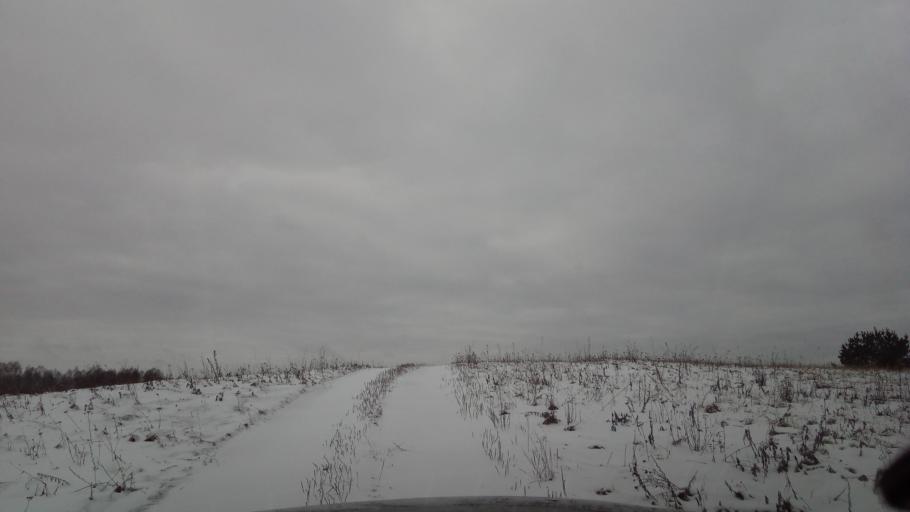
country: LT
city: Zarasai
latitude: 55.6882
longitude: 26.0936
